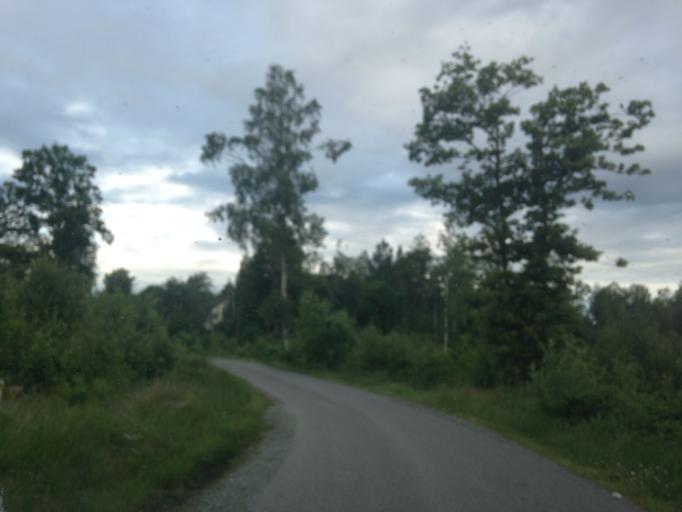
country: SE
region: Vaestra Goetaland
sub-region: Goteborg
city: Torslanda
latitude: 57.7781
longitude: 11.8509
